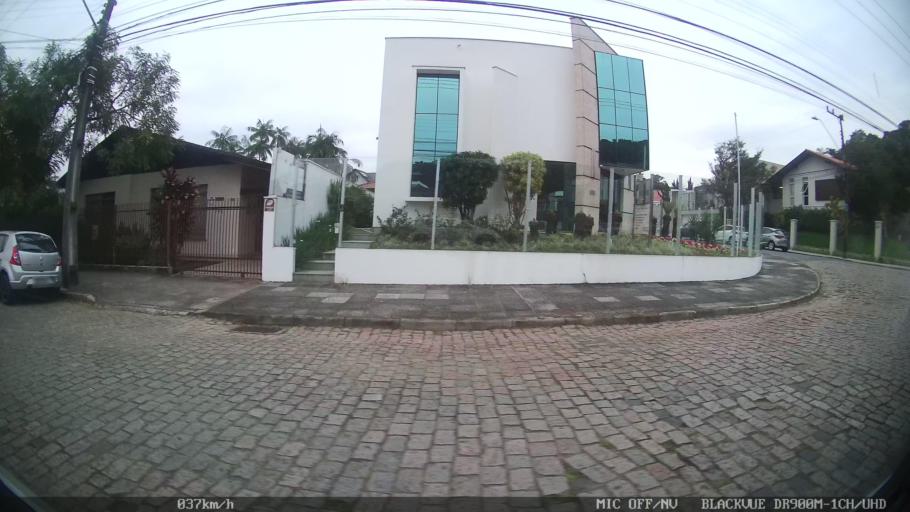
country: BR
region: Santa Catarina
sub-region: Joinville
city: Joinville
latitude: -26.3018
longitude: -48.8597
